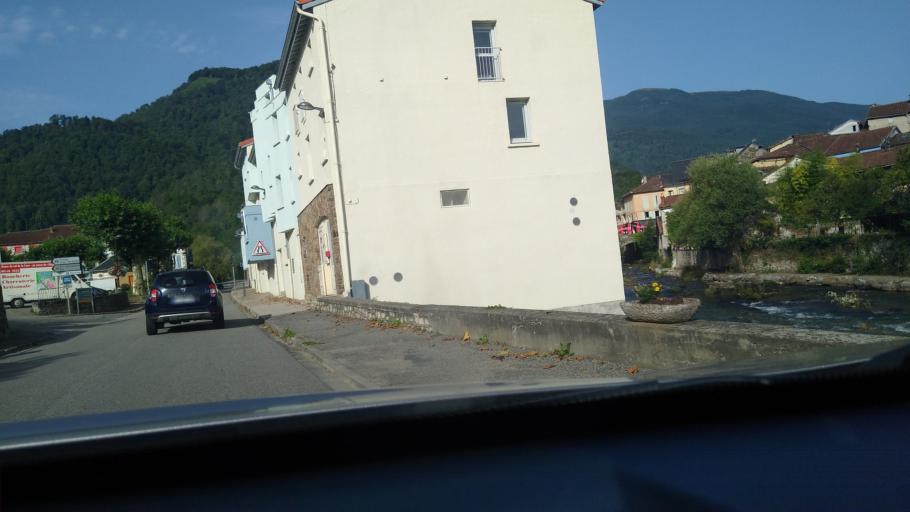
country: FR
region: Midi-Pyrenees
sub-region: Departement de l'Ariege
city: Saint-Girons
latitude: 42.8640
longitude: 1.2030
